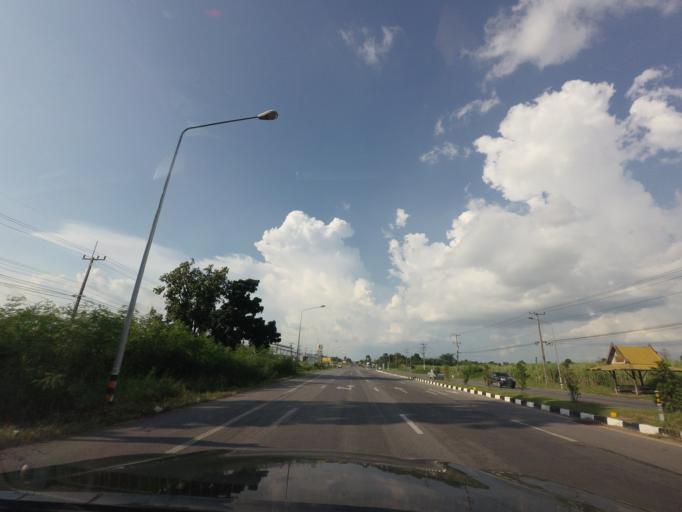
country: TH
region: Khon Kaen
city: Ban Haet
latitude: 16.1640
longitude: 102.7540
